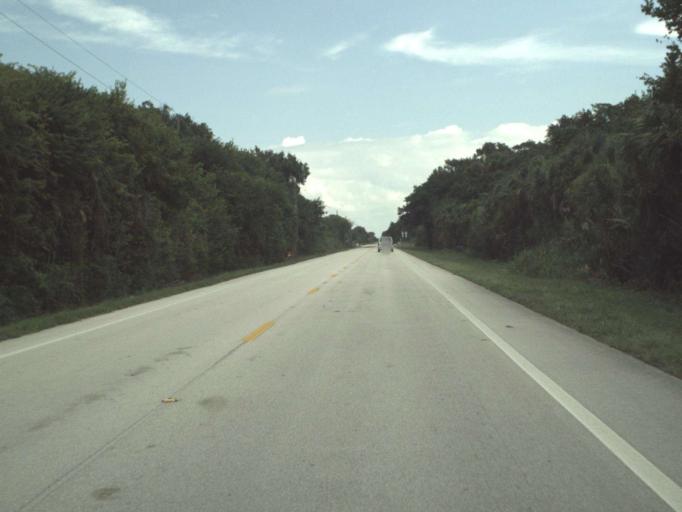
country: US
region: Florida
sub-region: Martin County
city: Indiantown
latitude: 27.0088
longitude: -80.6252
